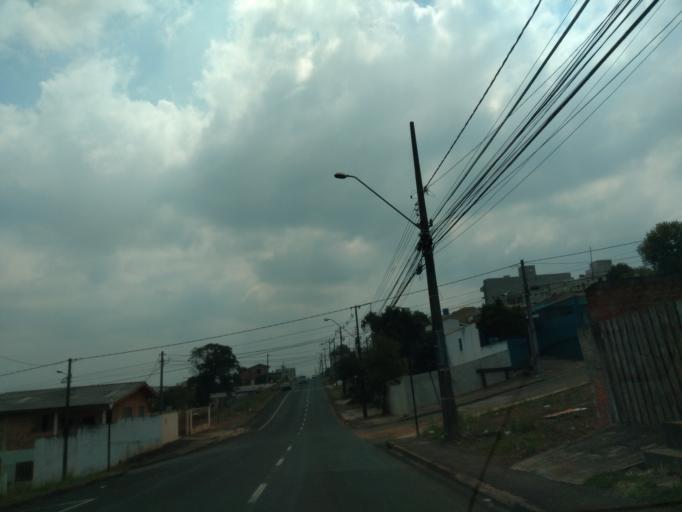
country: BR
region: Parana
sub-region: Guarapuava
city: Guarapuava
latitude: -25.3816
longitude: -51.4820
